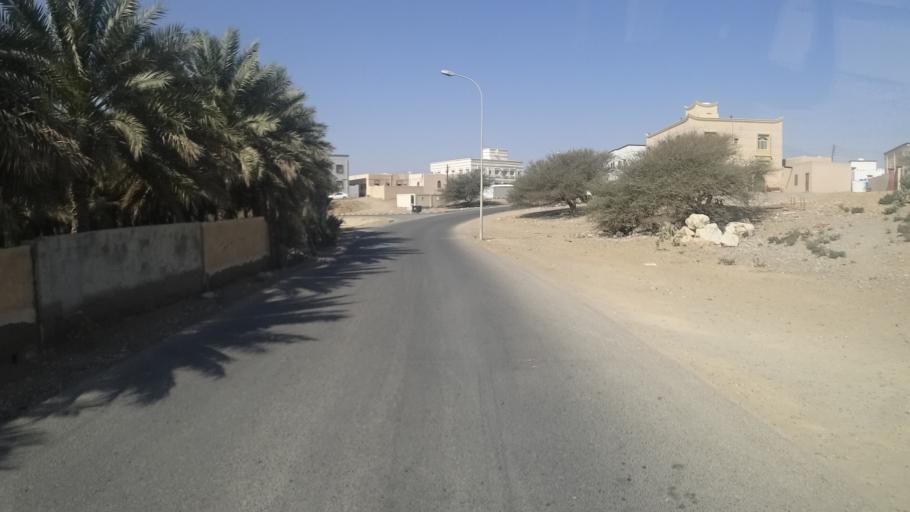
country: OM
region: Ash Sharqiyah
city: Sur
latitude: 22.5400
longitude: 59.4866
